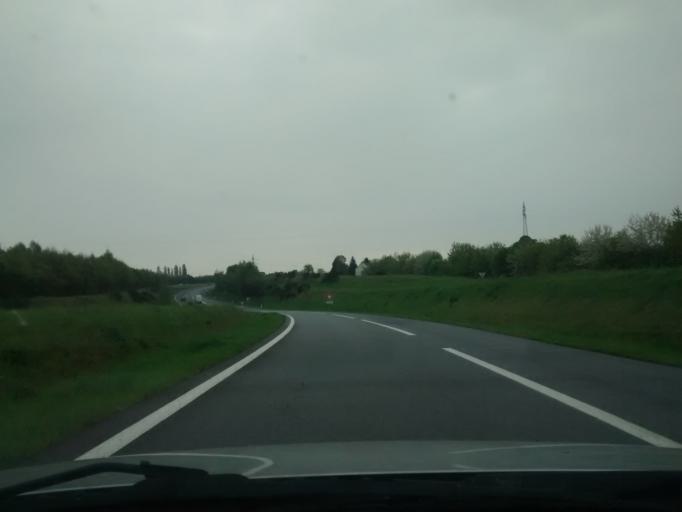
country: FR
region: Brittany
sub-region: Departement d'Ille-et-Vilaine
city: Cesson-Sevigne
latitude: 48.1138
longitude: -1.5712
